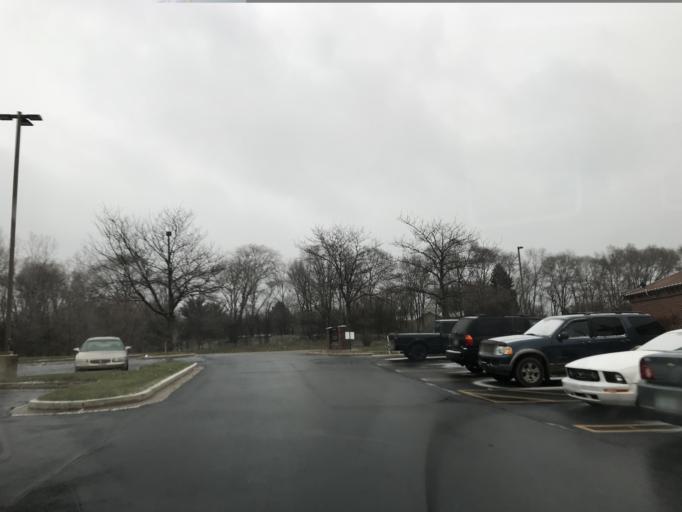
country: US
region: Michigan
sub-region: Oakland County
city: Farmington
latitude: 42.4286
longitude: -83.4216
